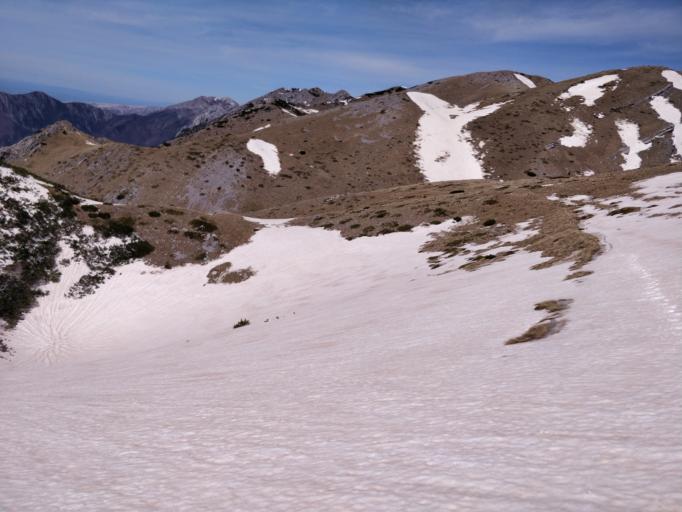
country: HR
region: Zadarska
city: Starigrad
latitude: 44.3360
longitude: 15.5542
